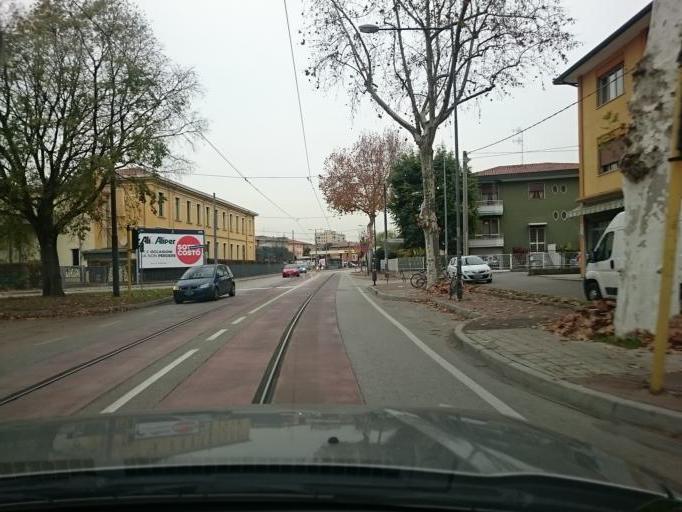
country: IT
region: Veneto
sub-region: Provincia di Padova
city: Mandriola-Sant'Agostino
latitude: 45.3733
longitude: 11.8710
